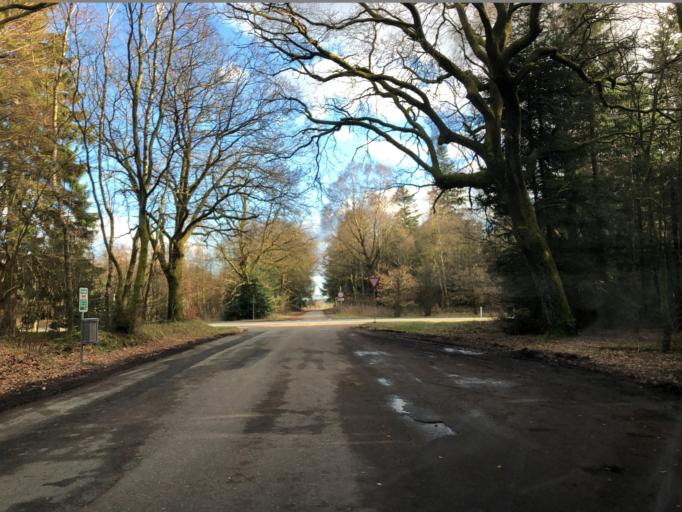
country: DK
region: Central Jutland
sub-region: Viborg Kommune
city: Karup
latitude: 56.3091
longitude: 9.2762
